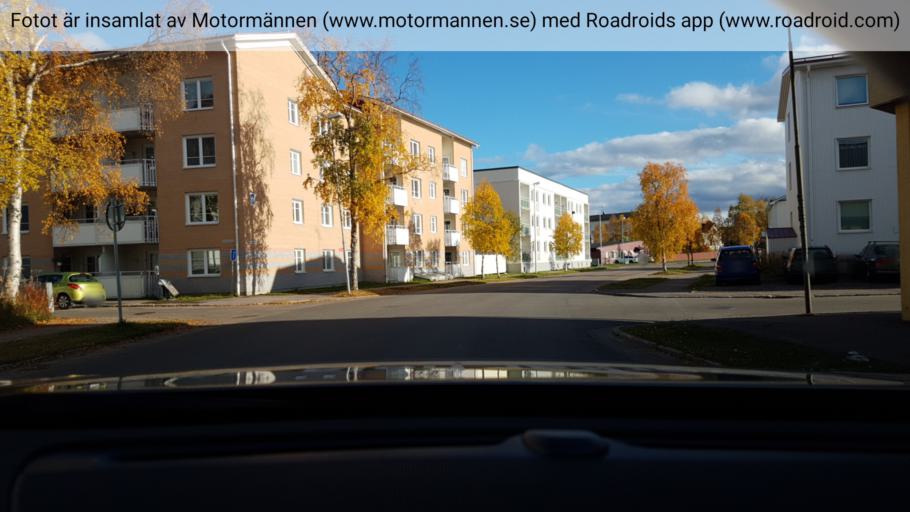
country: SE
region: Norrbotten
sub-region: Gallivare Kommun
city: Gaellivare
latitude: 67.1348
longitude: 20.6653
